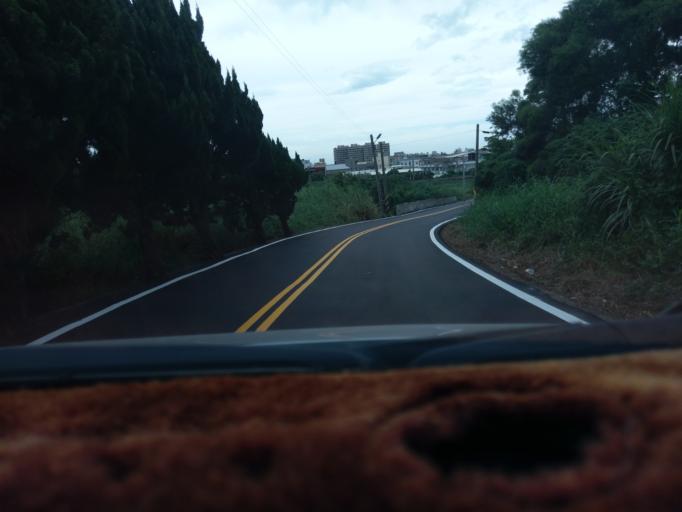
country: TW
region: Taiwan
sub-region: Hsinchu
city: Hsinchu
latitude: 24.7902
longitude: 120.9414
